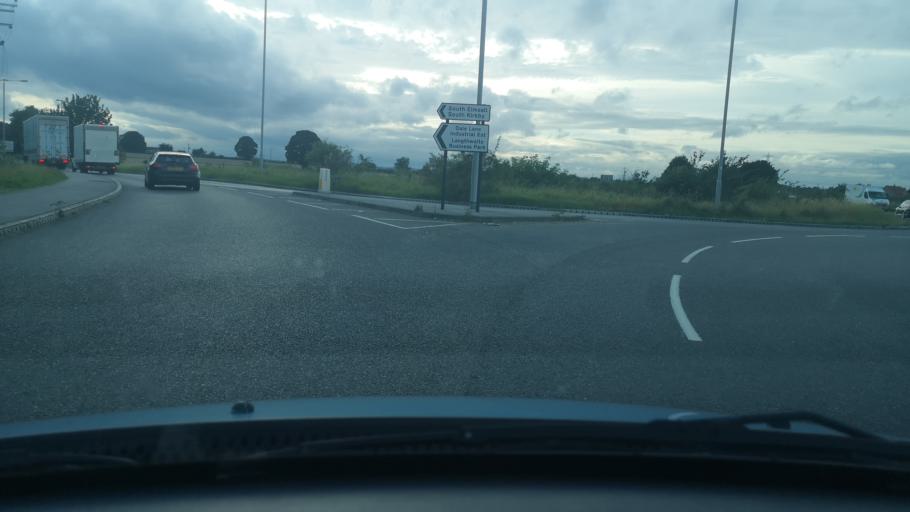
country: GB
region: England
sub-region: City and Borough of Wakefield
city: North Elmsall
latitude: 53.6065
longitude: -1.2769
